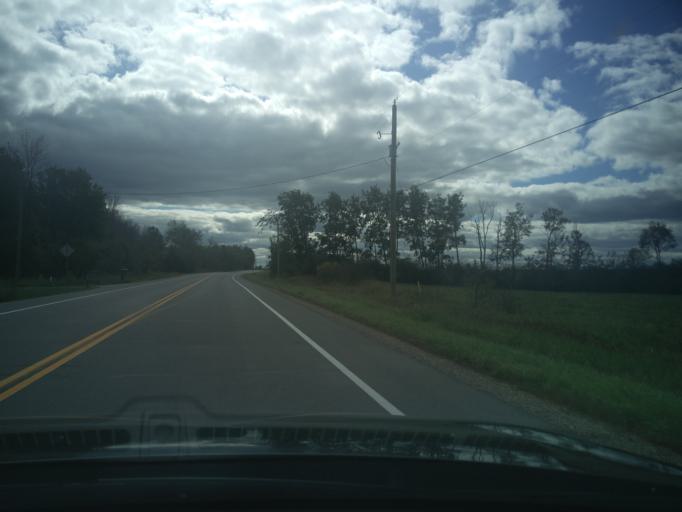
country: CA
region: Ontario
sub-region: Lanark County
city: Smiths Falls
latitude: 44.9984
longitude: -76.1006
